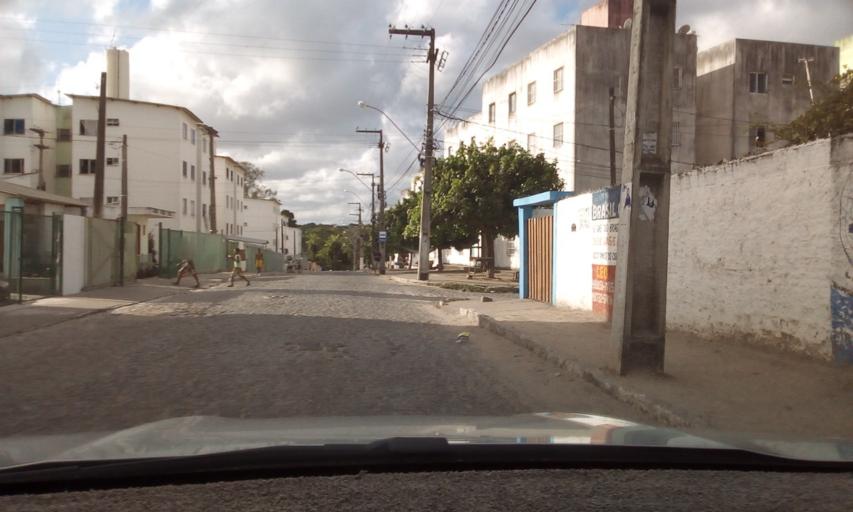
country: BR
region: Paraiba
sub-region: Bayeux
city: Bayeux
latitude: -7.1699
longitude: -34.9152
